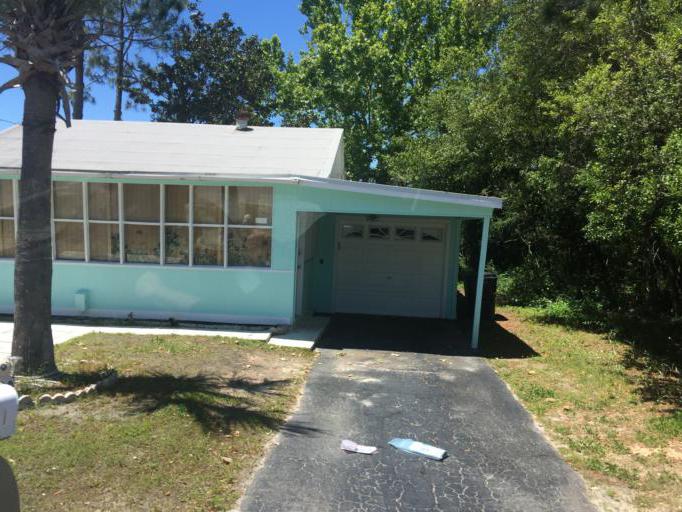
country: US
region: Florida
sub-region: Bay County
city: Laguna Beach
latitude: 30.2497
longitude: -85.9384
